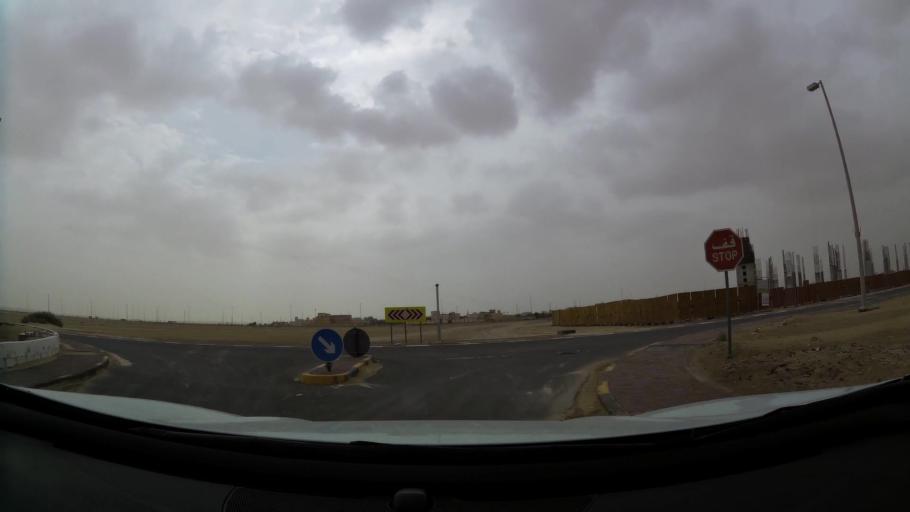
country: AE
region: Abu Dhabi
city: Abu Dhabi
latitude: 24.3654
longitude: 54.6655
